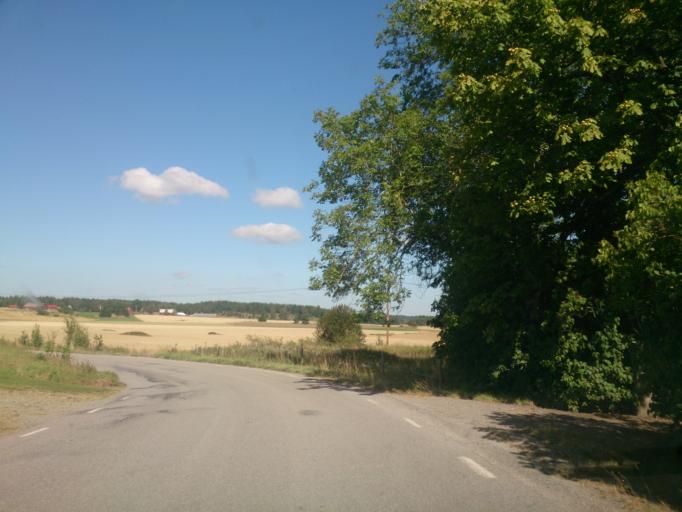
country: SE
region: OEstergoetland
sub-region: Norrkopings Kommun
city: Krokek
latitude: 58.5349
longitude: 16.6090
